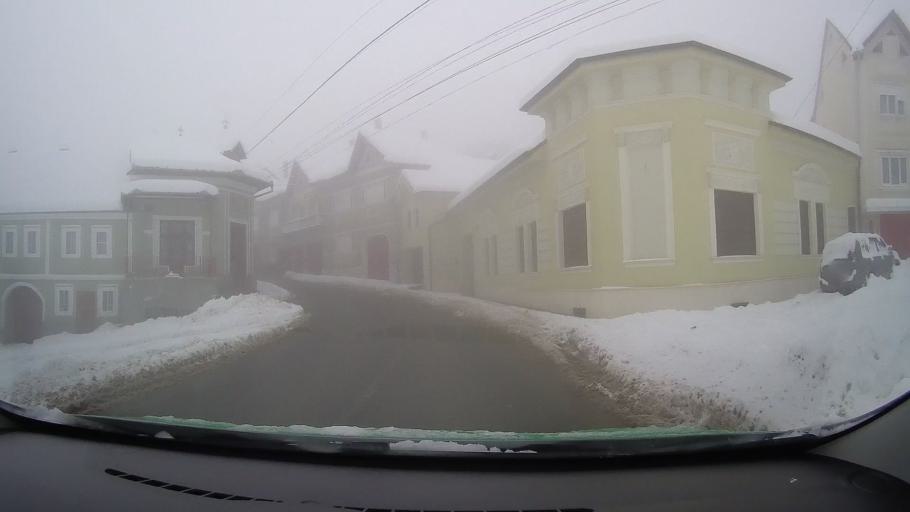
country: RO
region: Sibiu
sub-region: Comuna Poiana Sibiului
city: Poiana Sibiului
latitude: 45.8086
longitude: 23.7305
